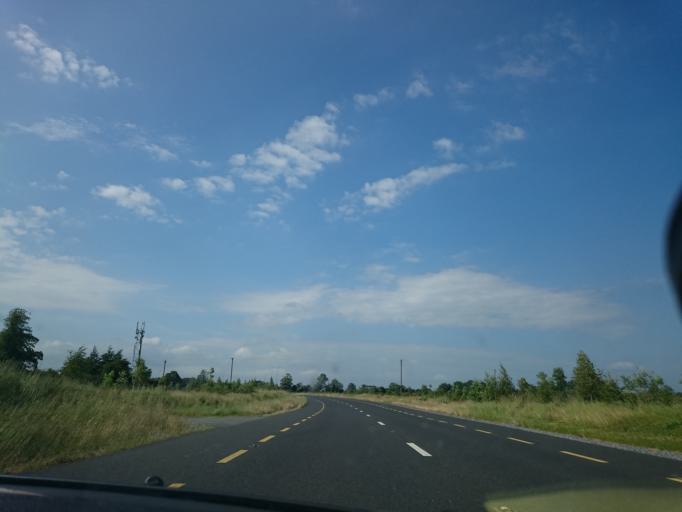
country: IE
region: Leinster
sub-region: Kilkenny
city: Kilkenny
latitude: 52.5686
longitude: -7.2296
